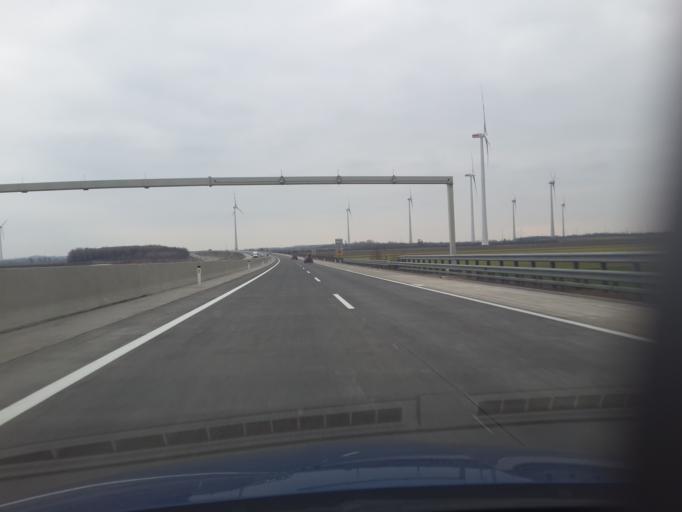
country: AT
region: Burgenland
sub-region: Politischer Bezirk Neusiedl am See
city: Pama
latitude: 48.0598
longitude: 17.0028
